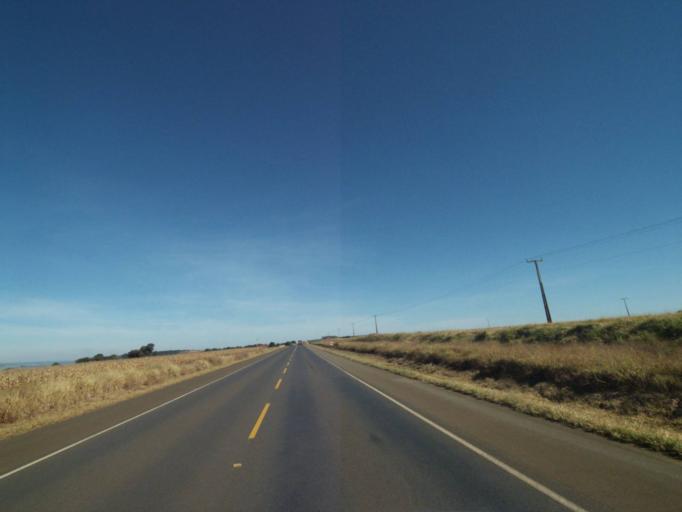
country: BR
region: Parana
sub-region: Tibagi
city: Tibagi
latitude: -24.3537
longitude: -50.3155
